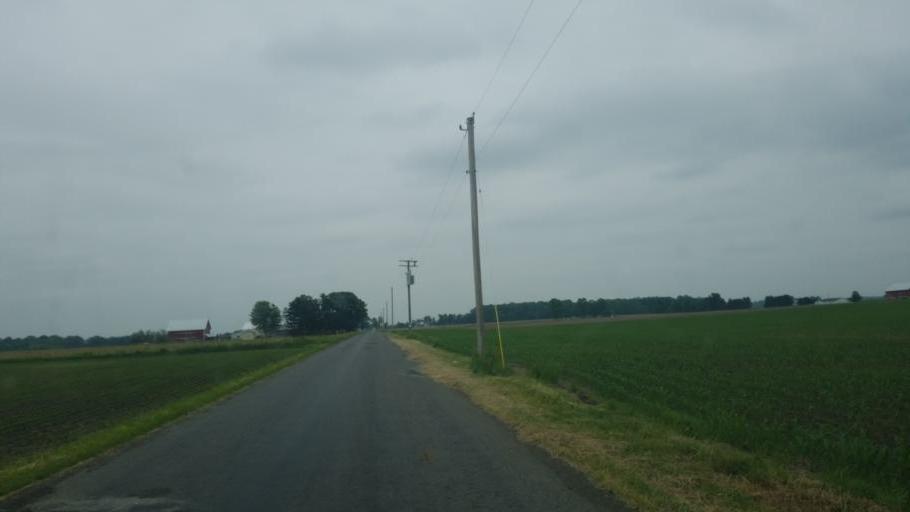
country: US
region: Indiana
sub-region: Elkhart County
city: Wakarusa
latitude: 41.4935
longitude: -86.0653
